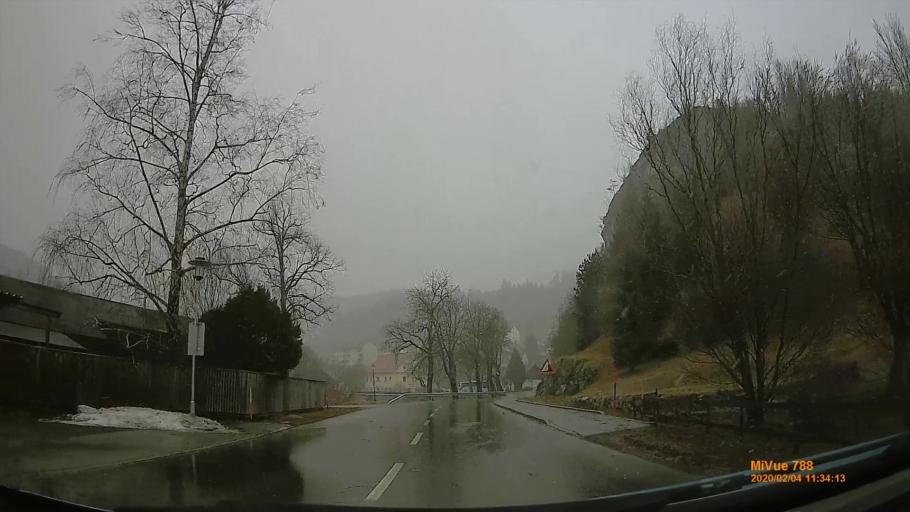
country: AT
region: Styria
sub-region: Politischer Bezirk Bruck-Muerzzuschlag
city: Neuberg an der Muerz
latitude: 47.6684
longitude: 15.5742
